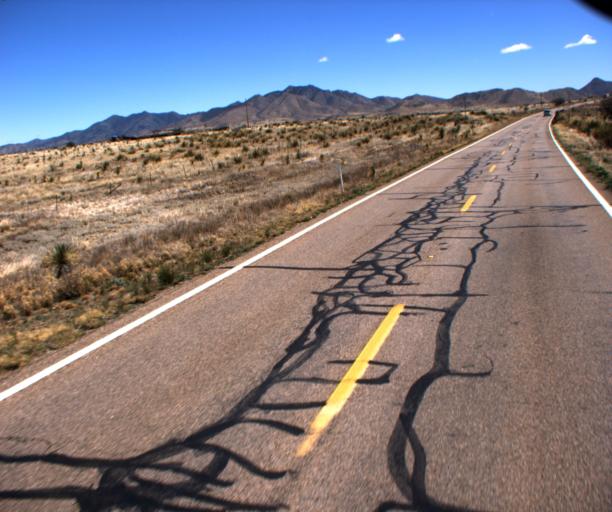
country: US
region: Arizona
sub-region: Cochise County
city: Huachuca City
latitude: 31.7233
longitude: -110.5299
